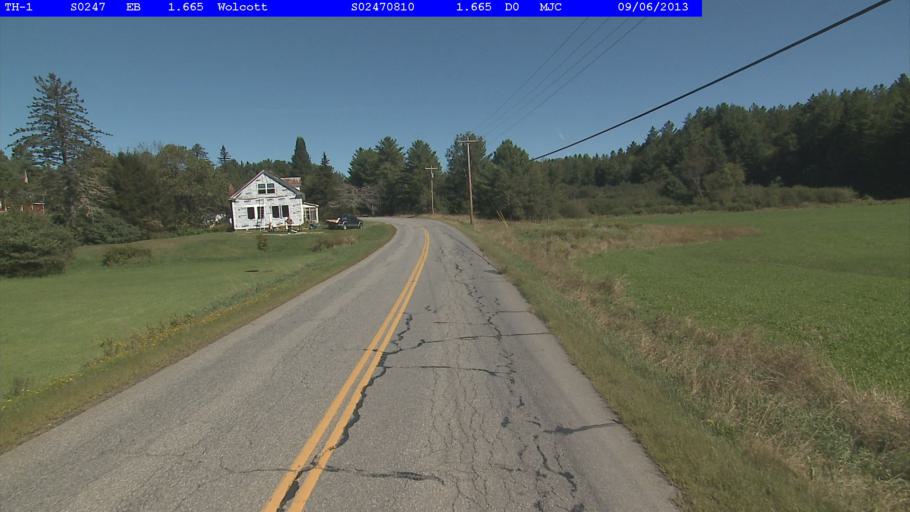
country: US
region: Vermont
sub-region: Lamoille County
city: Morrisville
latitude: 44.5798
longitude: -72.4758
